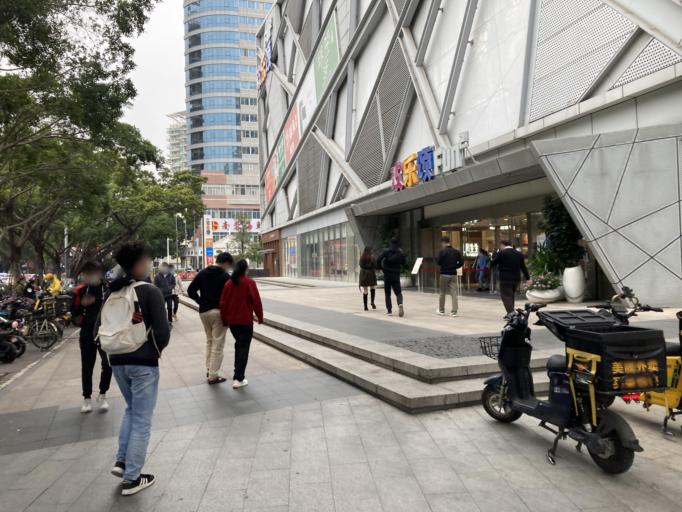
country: CN
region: Guangdong
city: Nantou
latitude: 22.5381
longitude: 113.9148
